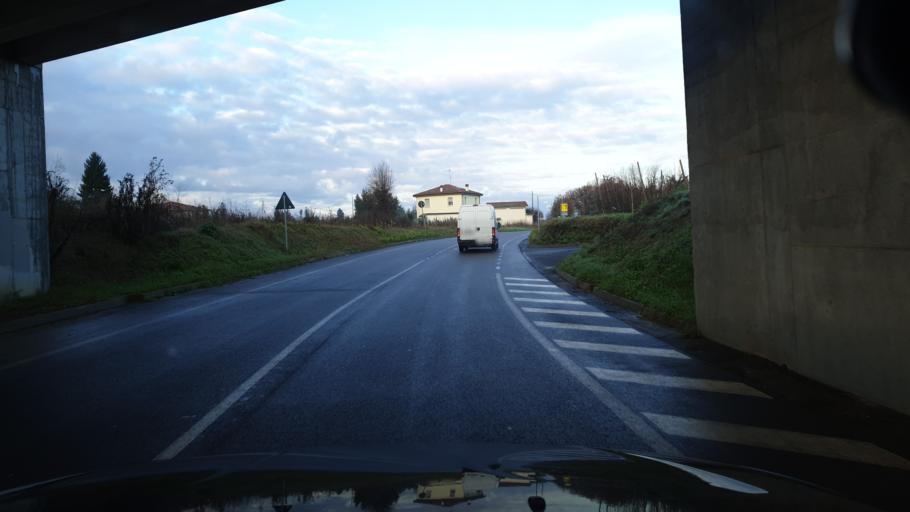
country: IT
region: Emilia-Romagna
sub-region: Provincia di Bologna
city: Crespellano
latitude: 44.5210
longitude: 11.1234
